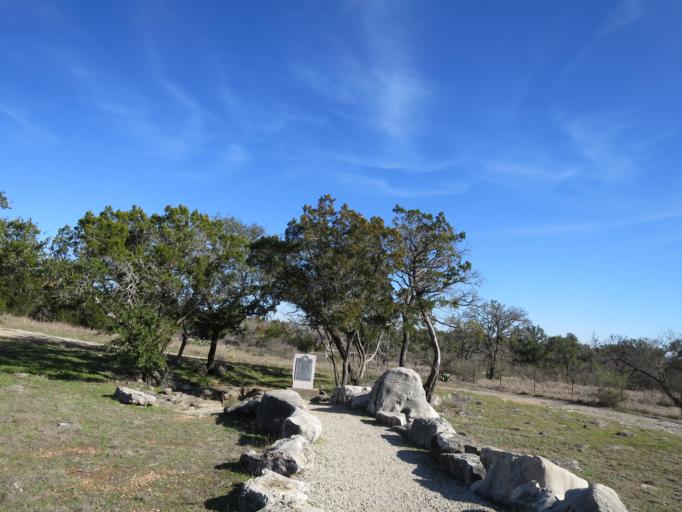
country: US
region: Texas
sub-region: Burnet County
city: Meadowlakes
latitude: 30.5285
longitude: -98.2651
